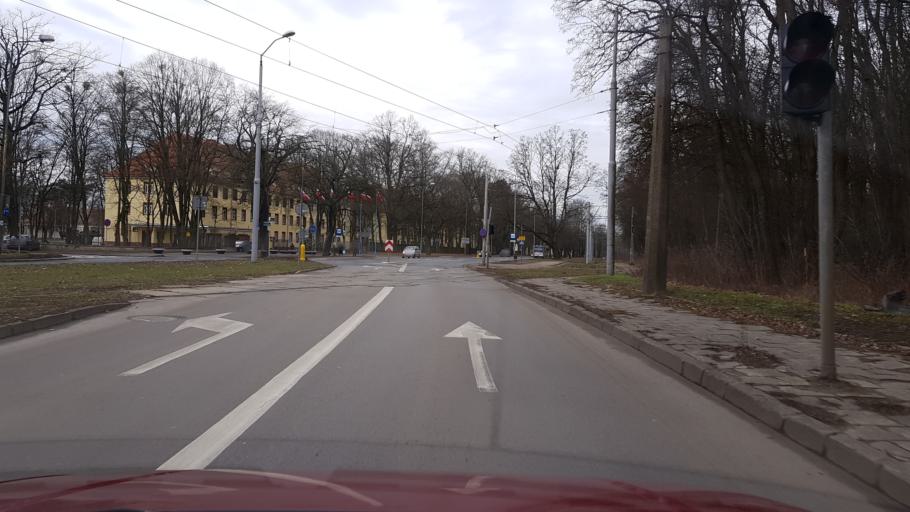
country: PL
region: West Pomeranian Voivodeship
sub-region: Szczecin
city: Szczecin
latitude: 53.4609
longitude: 14.4987
